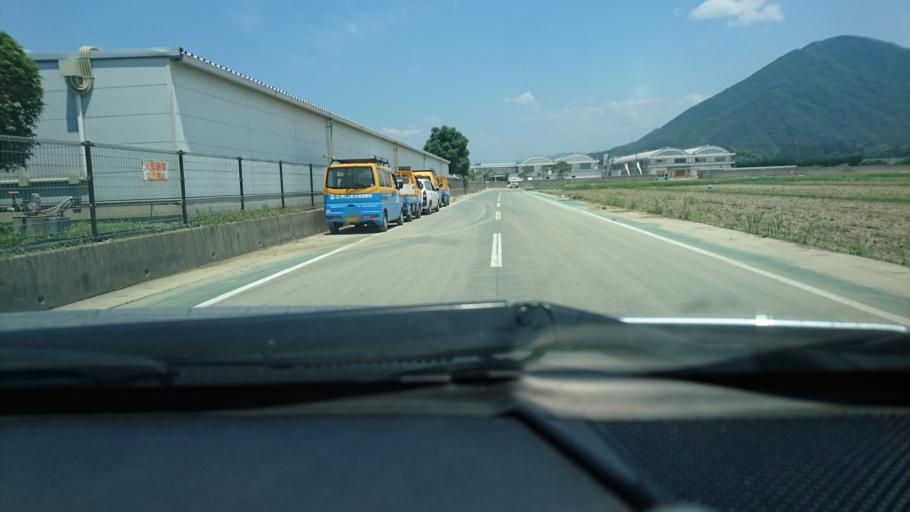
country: JP
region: Ehime
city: Ozu
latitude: 33.5267
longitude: 132.5675
